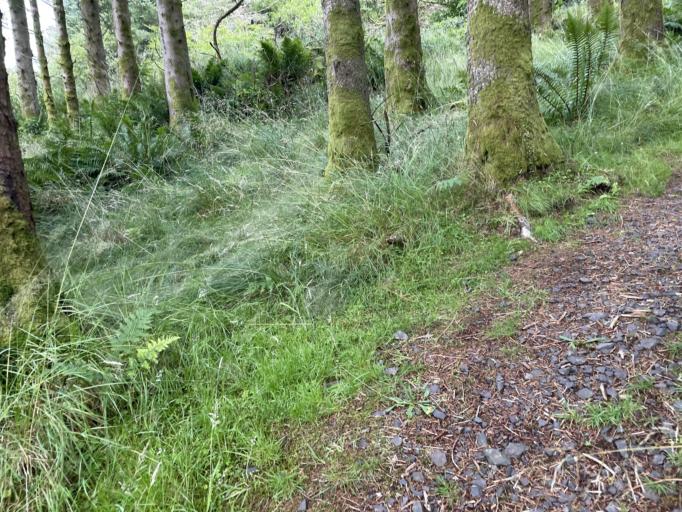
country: GB
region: Scotland
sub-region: South Ayrshire
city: Maybole
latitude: 55.2069
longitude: -4.6734
